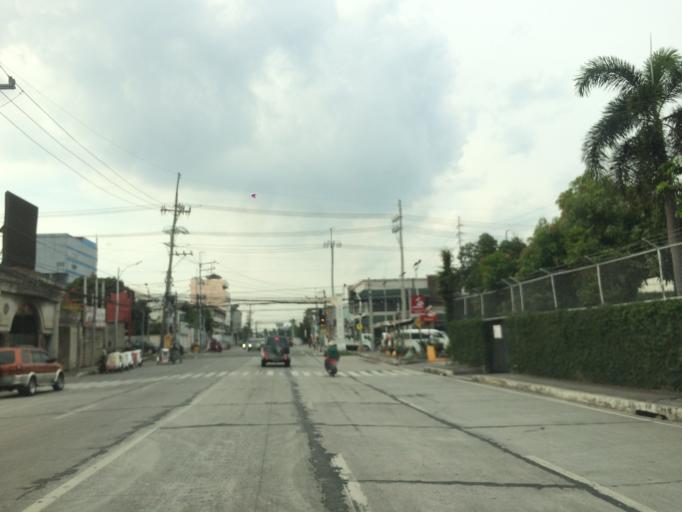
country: PH
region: Calabarzon
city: Del Monte
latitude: 14.6382
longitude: 121.0055
